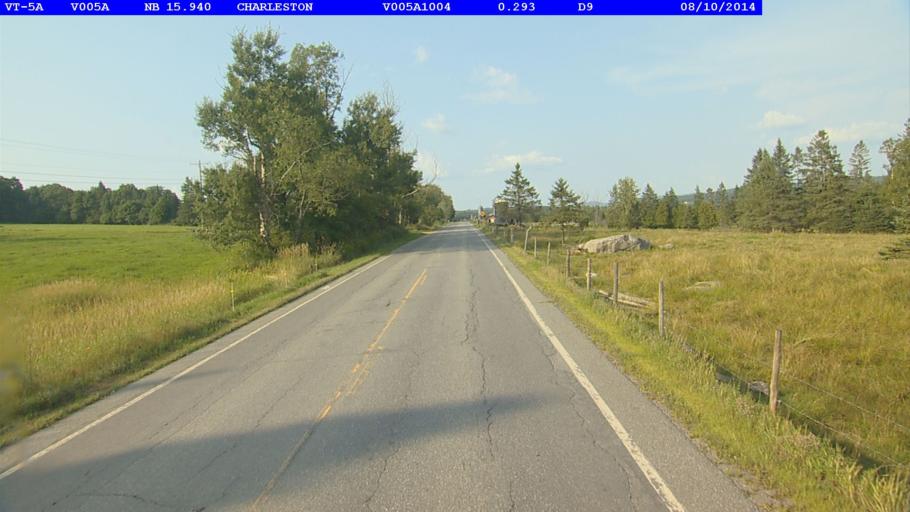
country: US
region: Vermont
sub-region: Orleans County
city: Newport
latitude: 44.8385
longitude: -72.0628
